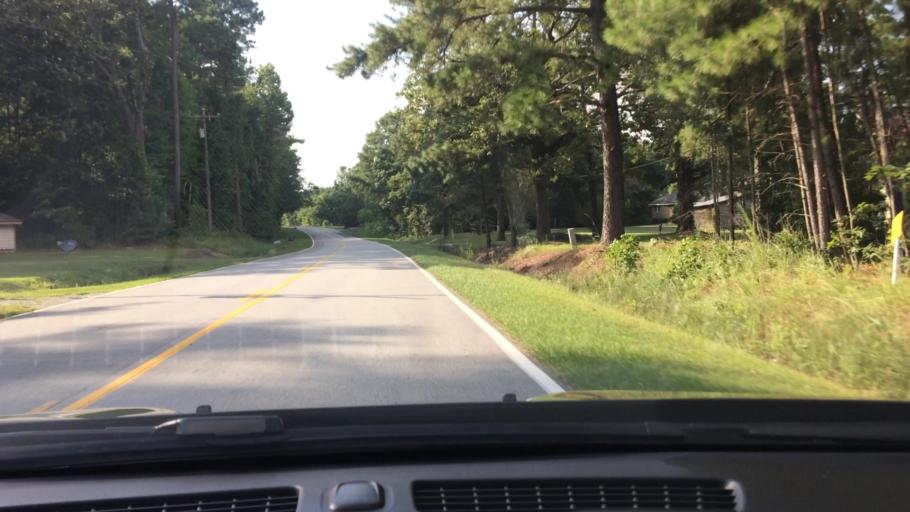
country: US
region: North Carolina
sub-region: Beaufort County
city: River Road
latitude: 35.4491
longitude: -77.0159
